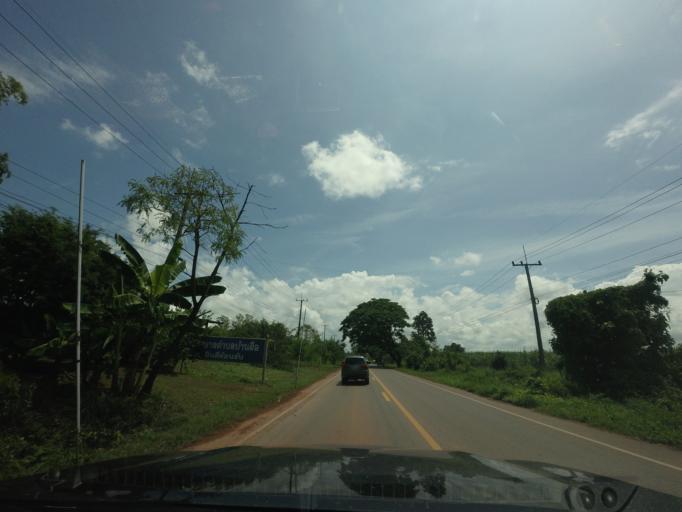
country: TH
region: Changwat Udon Thani
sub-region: Amphoe Ban Phue
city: Ban Phue
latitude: 17.6978
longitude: 102.4498
